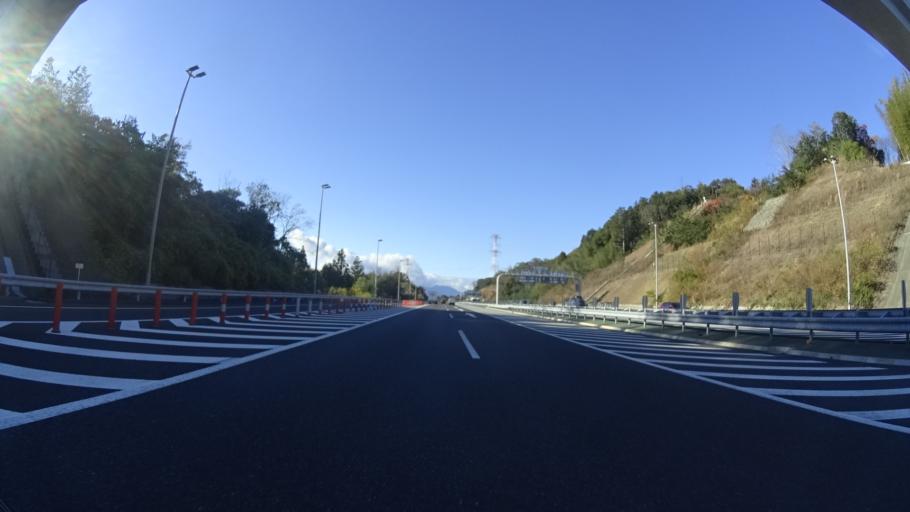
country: JP
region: Mie
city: Yokkaichi
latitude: 35.0411
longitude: 136.6231
